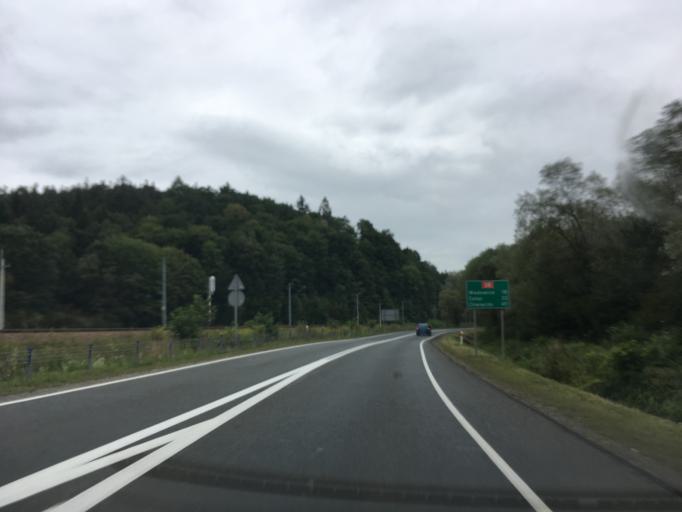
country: PL
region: Lesser Poland Voivodeship
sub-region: Powiat suski
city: Zembrzyce
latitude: 49.7674
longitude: 19.5927
